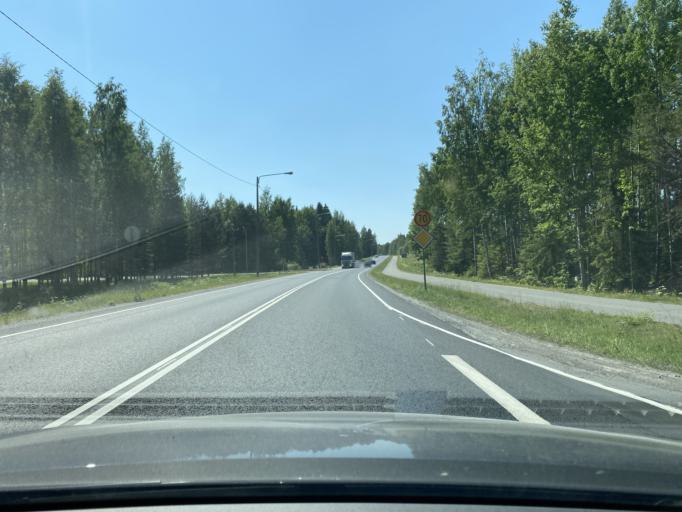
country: FI
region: Pirkanmaa
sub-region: Tampere
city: Nokia
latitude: 61.4633
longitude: 23.5034
